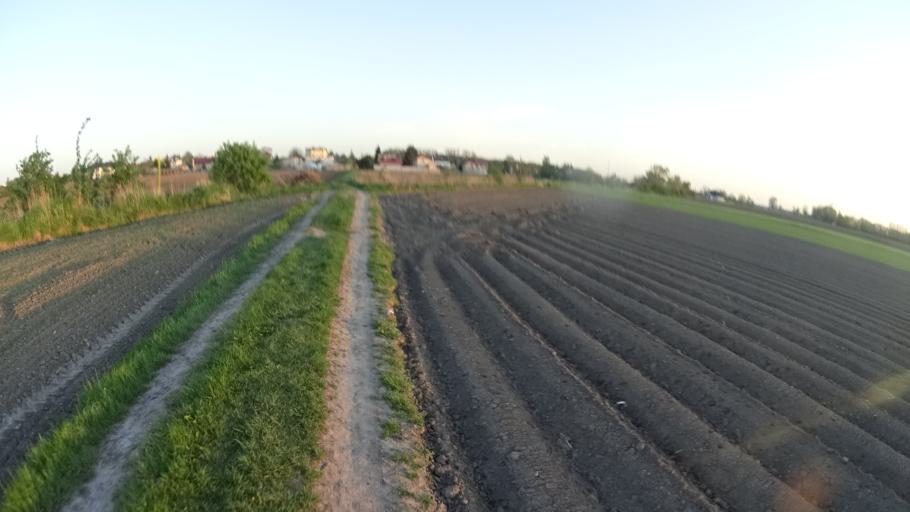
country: PL
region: Masovian Voivodeship
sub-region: Powiat warszawski zachodni
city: Ozarow Mazowiecki
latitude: 52.2251
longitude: 20.7813
